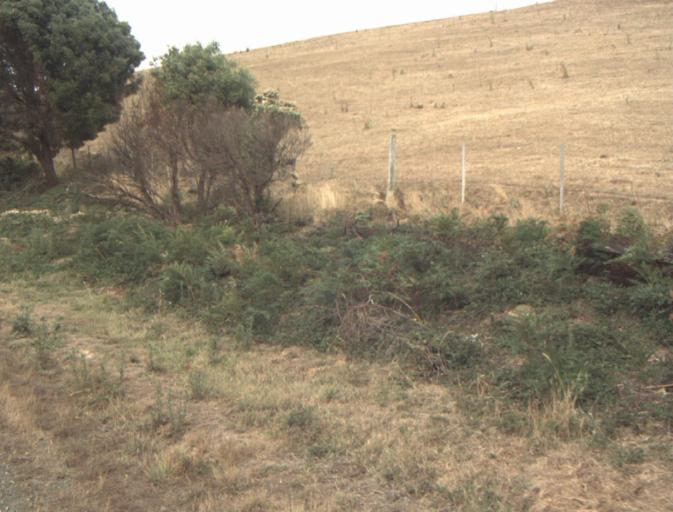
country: AU
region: Tasmania
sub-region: Dorset
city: Bridport
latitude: -41.1848
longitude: 147.2621
